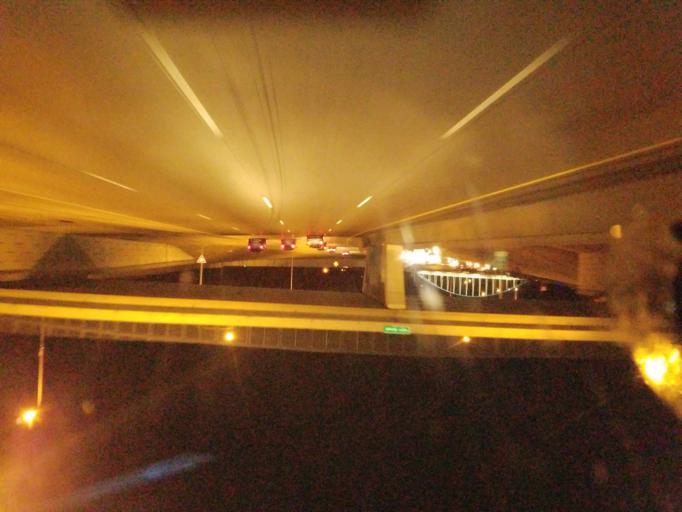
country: US
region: Iowa
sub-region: Polk County
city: Windsor Heights
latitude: 41.5912
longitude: -93.6751
